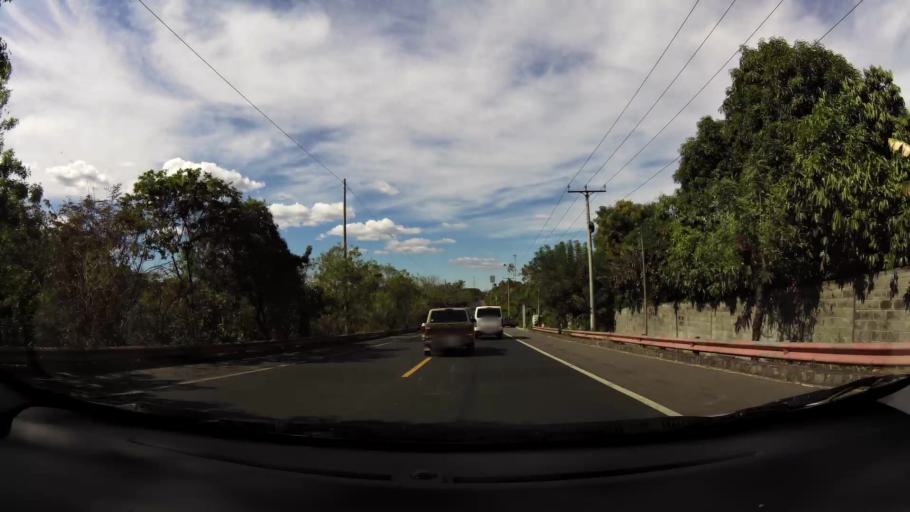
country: SV
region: San Salvador
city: Guazapa
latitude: 13.8667
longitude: -89.1685
